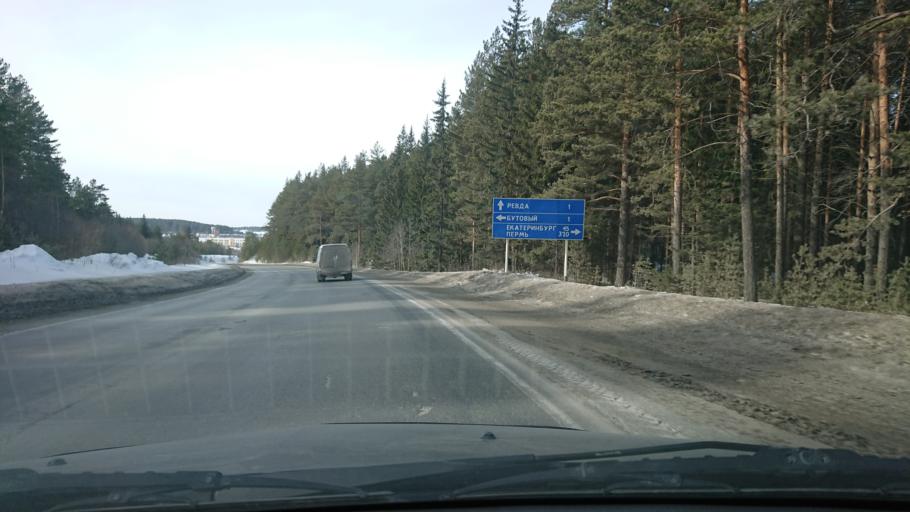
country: RU
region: Sverdlovsk
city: Revda
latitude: 56.7973
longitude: 59.9920
